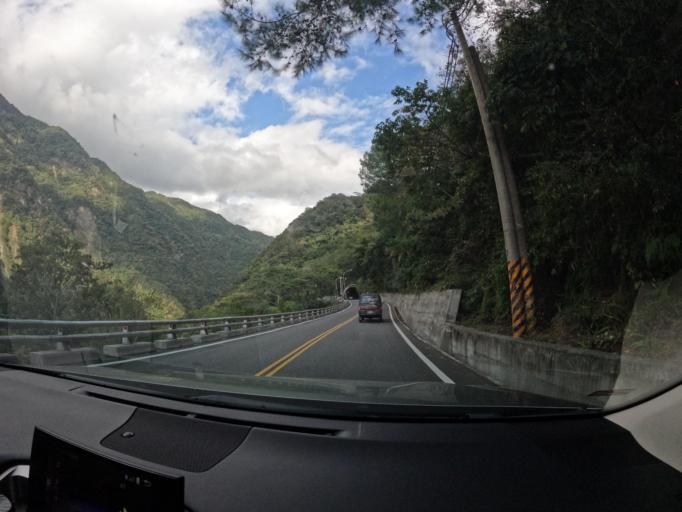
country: TW
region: Taiwan
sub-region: Taitung
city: Taitung
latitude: 23.1506
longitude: 121.0756
